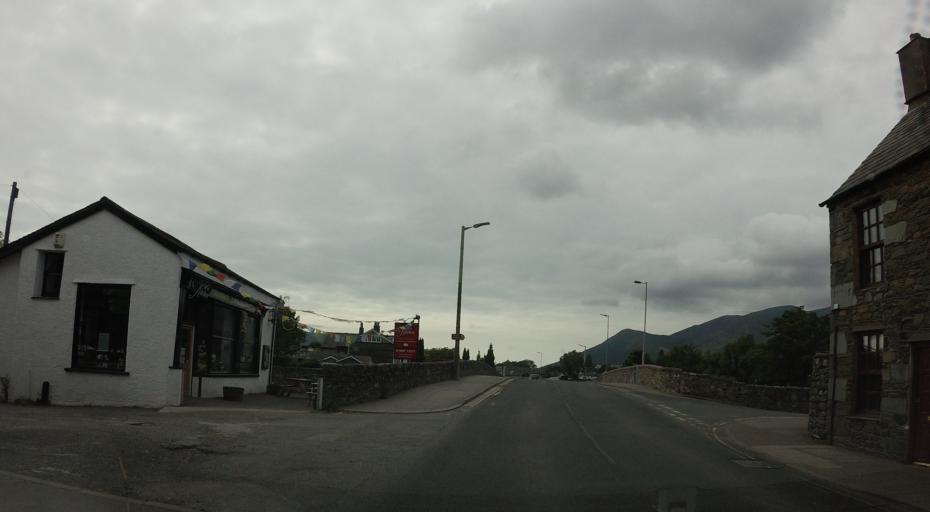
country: GB
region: England
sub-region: Cumbria
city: Keswick
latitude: 54.6031
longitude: -3.1420
